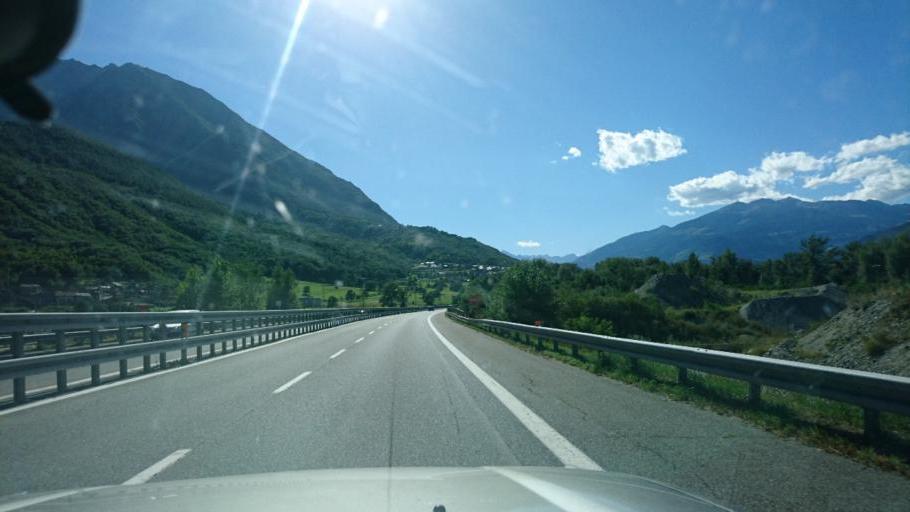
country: IT
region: Aosta Valley
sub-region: Valle d'Aosta
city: Saint Marcel
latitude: 45.7344
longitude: 7.4346
